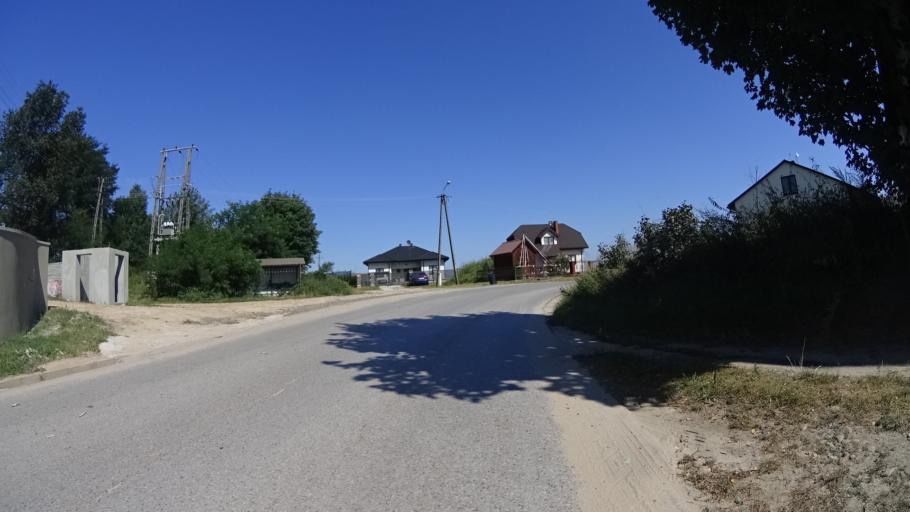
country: PL
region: Masovian Voivodeship
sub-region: Powiat bialobrzeski
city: Wysmierzyce
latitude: 51.6564
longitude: 20.8231
